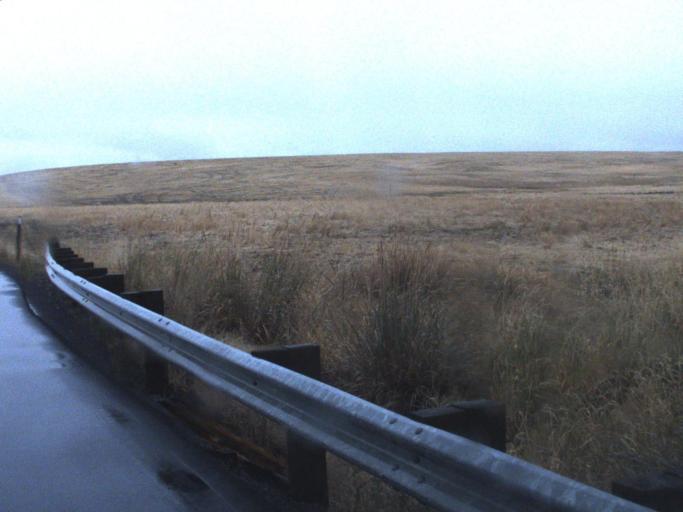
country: US
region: Washington
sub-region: Lincoln County
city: Davenport
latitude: 47.3837
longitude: -118.1354
